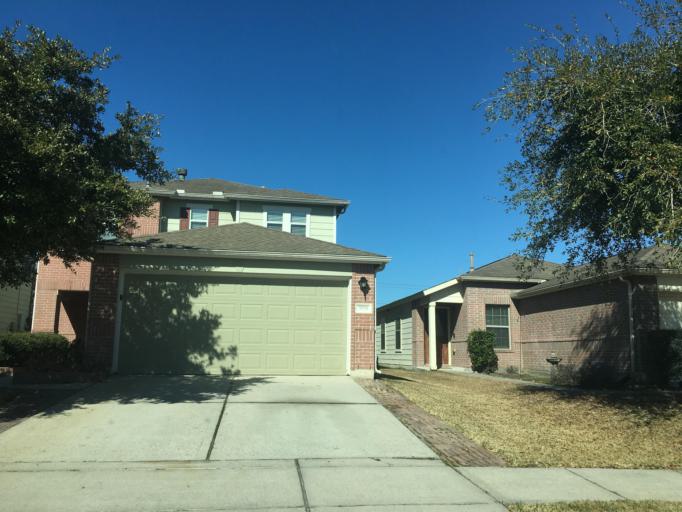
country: US
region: Texas
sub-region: Harris County
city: Spring
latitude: 30.0869
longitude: -95.4632
